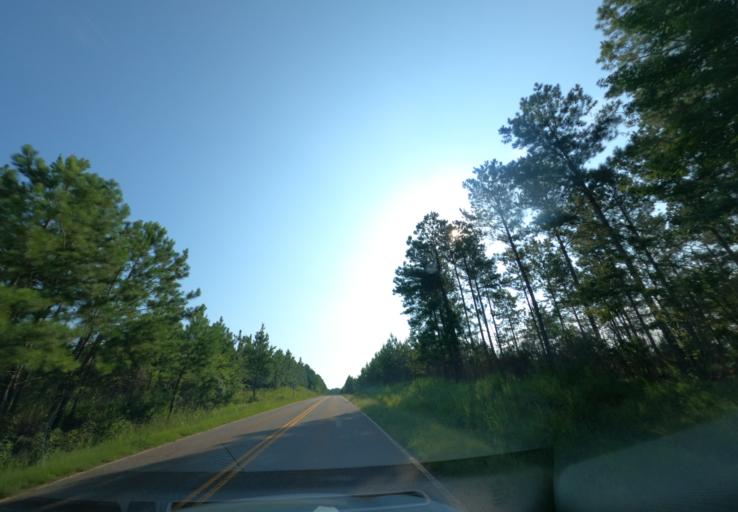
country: US
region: South Carolina
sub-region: Edgefield County
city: Edgefield
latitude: 33.7573
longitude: -81.9535
